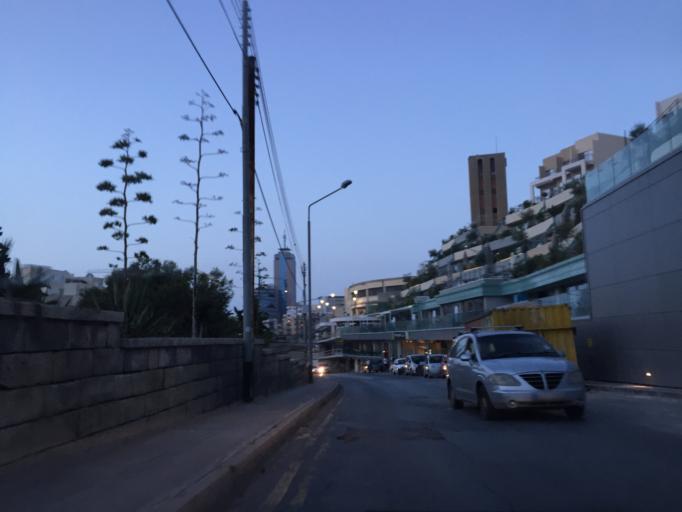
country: MT
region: Saint Julian
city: San Giljan
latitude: 35.9170
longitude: 14.4886
